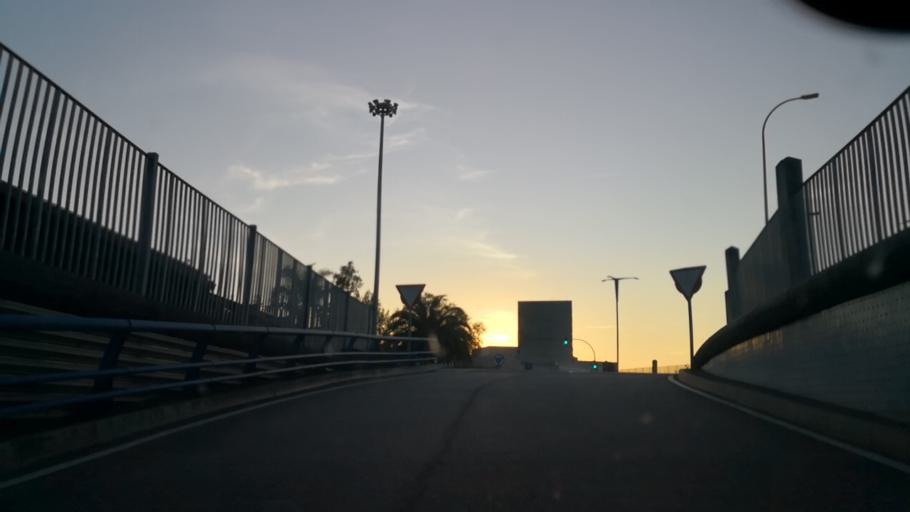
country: ES
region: Galicia
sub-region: Provincia de Pontevedra
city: Vigo
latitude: 42.2398
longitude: -8.7166
